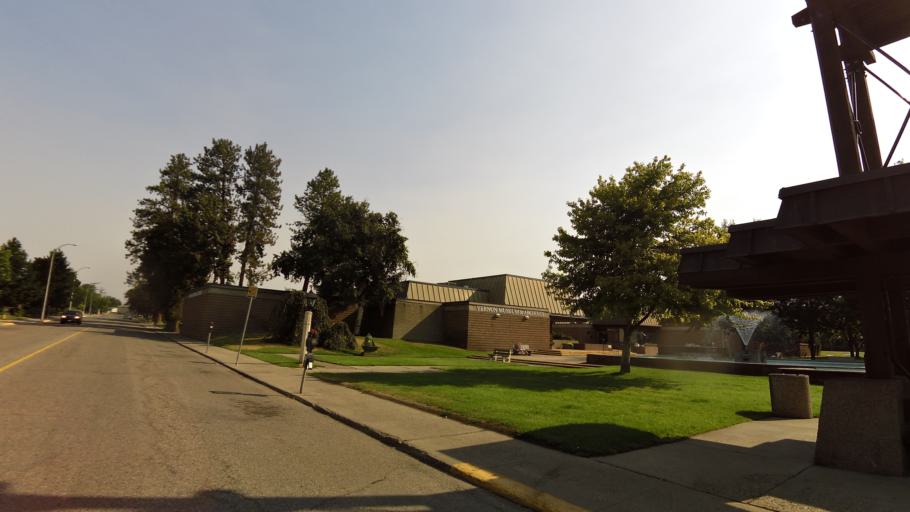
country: CA
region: British Columbia
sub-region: Regional District of North Okanagan
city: Vernon
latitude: 50.2654
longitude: -119.2723
